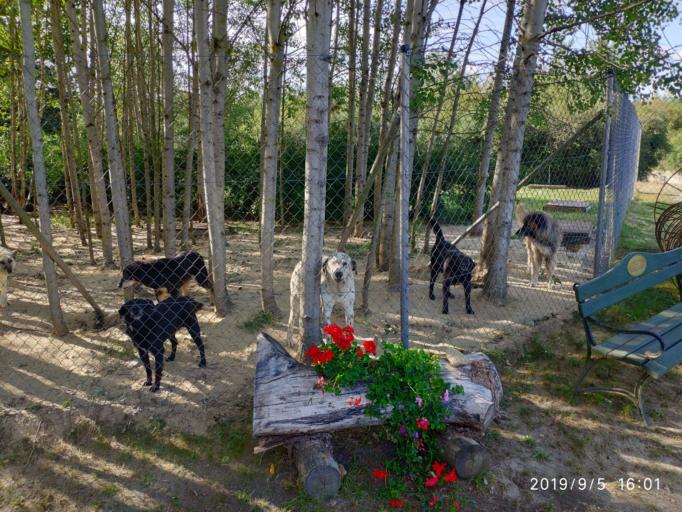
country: PL
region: Lubusz
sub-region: Powiat krosnienski
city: Dabie
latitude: 52.0157
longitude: 15.2233
